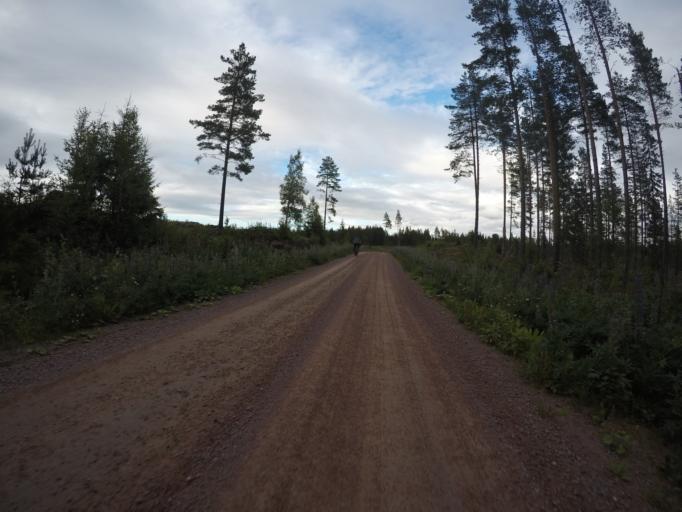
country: SE
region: OErebro
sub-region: Hallefors Kommun
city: Haellefors
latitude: 60.0391
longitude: 14.4968
